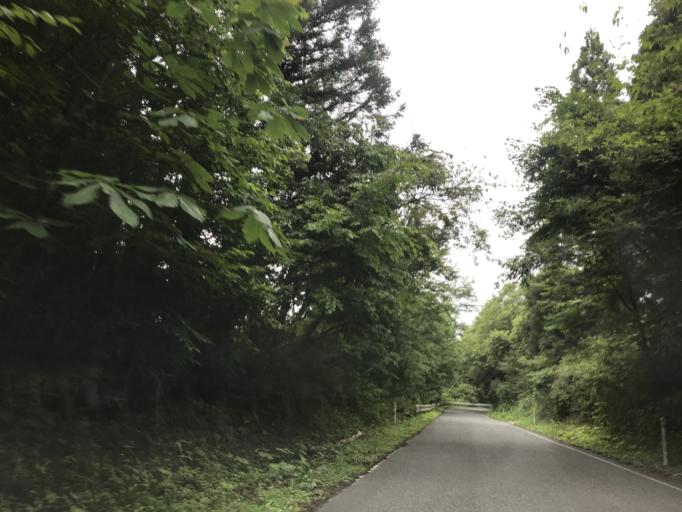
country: JP
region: Iwate
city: Ichinoseki
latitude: 38.8269
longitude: 141.2329
